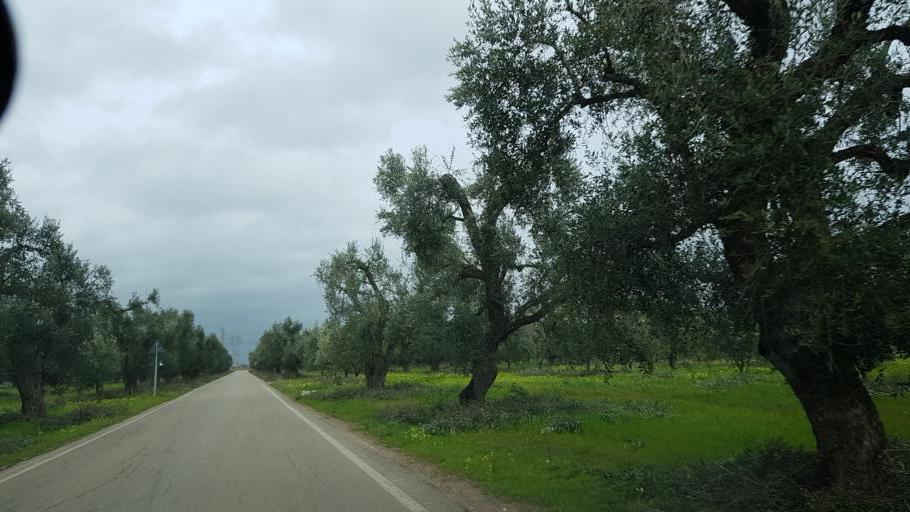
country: IT
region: Apulia
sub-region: Provincia di Brindisi
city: Brindisi
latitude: 40.5963
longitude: 17.9000
